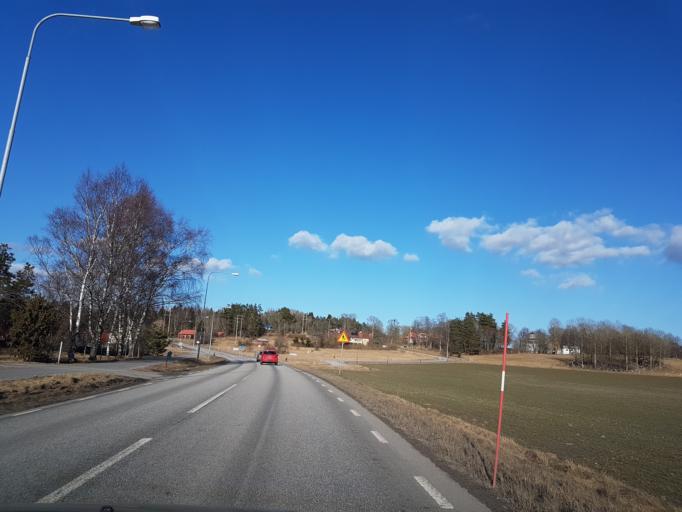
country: SE
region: Stockholm
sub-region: Norrtalje Kommun
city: Rimbo
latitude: 59.7473
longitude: 18.3822
